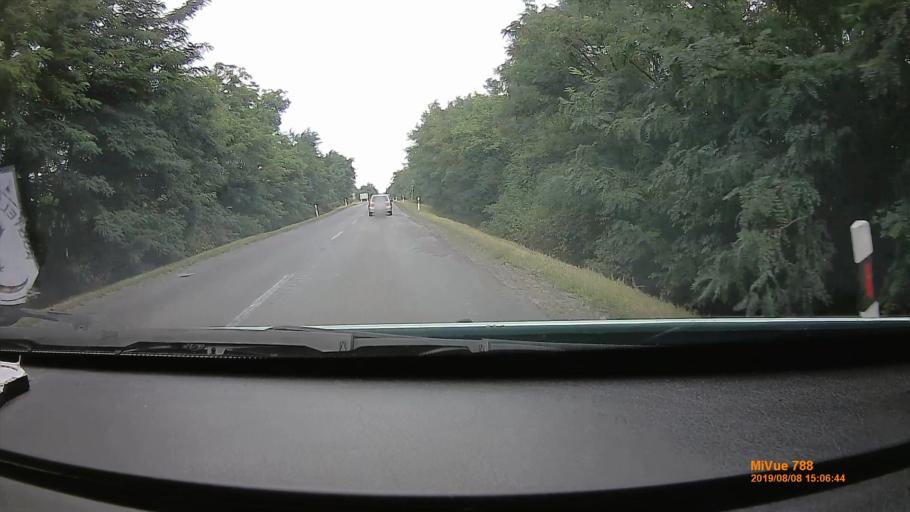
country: HU
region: Szabolcs-Szatmar-Bereg
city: Tunyogmatolcs
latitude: 47.9506
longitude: 22.4332
